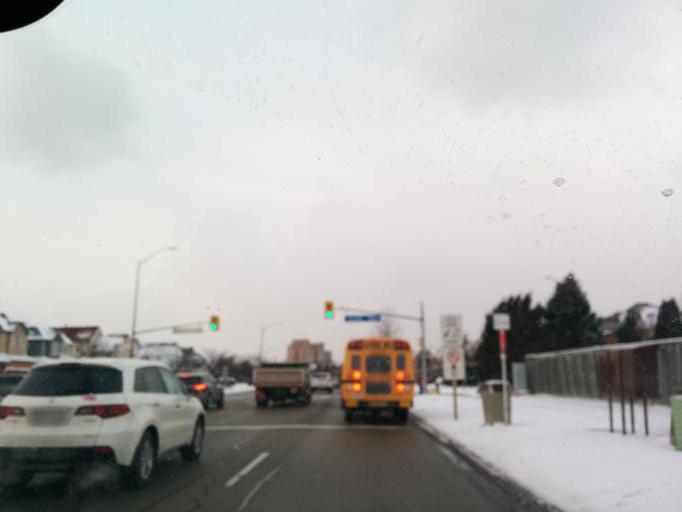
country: CA
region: Ontario
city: Mississauga
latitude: 43.5700
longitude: -79.7326
